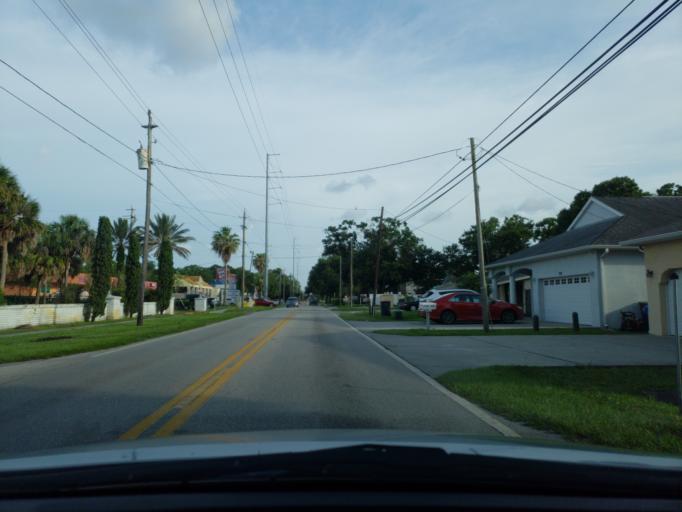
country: US
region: Florida
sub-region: Hillsborough County
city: Egypt Lake-Leto
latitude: 28.0141
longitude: -82.5008
